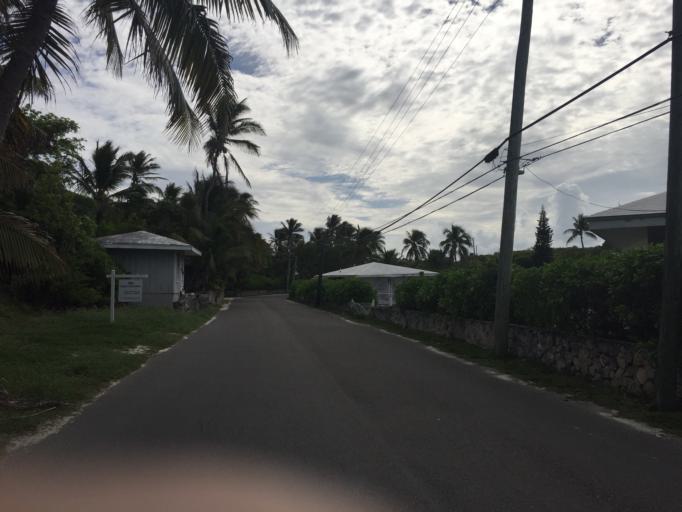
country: BS
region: Central Abaco
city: Marsh Harbour
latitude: 26.5307
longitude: -76.9612
